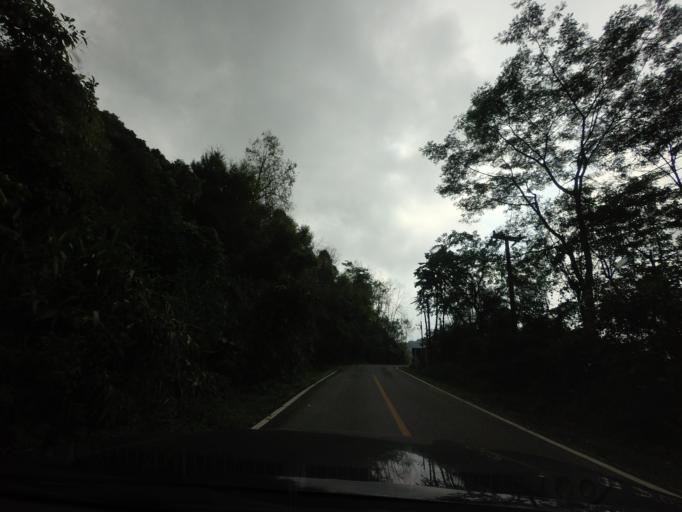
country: TH
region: Nan
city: Bo Kluea
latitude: 19.1858
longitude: 101.0774
